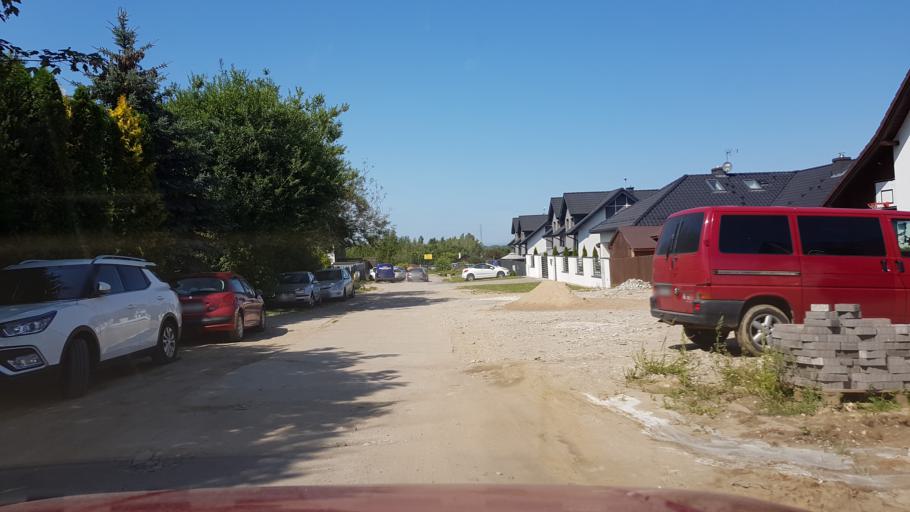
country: PL
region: West Pomeranian Voivodeship
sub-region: Koszalin
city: Koszalin
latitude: 54.2215
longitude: 16.1677
